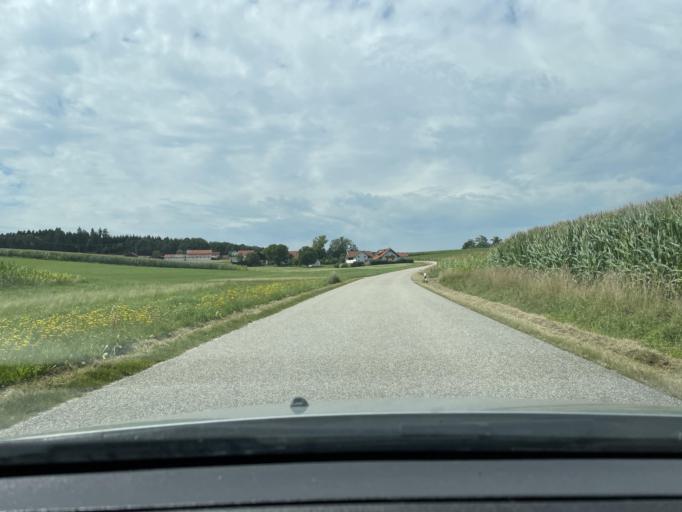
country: DE
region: Bavaria
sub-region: Lower Bavaria
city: Geisenhausen
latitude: 48.4419
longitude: 12.2483
